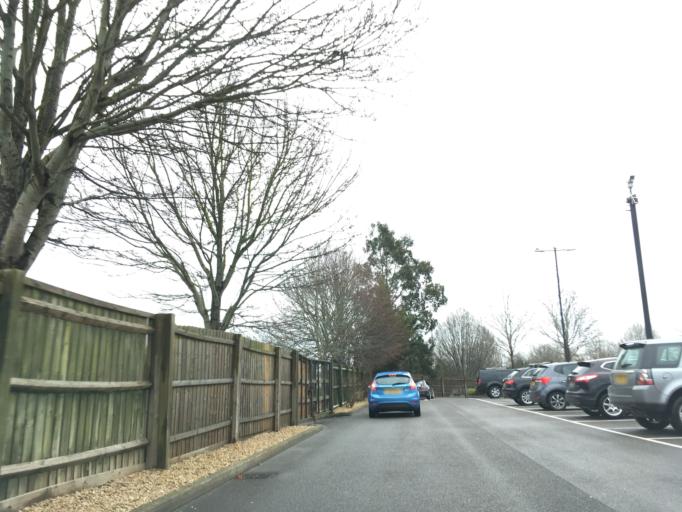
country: GB
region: England
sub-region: Borough of Swindon
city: Swindon
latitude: 51.5656
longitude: -1.7977
